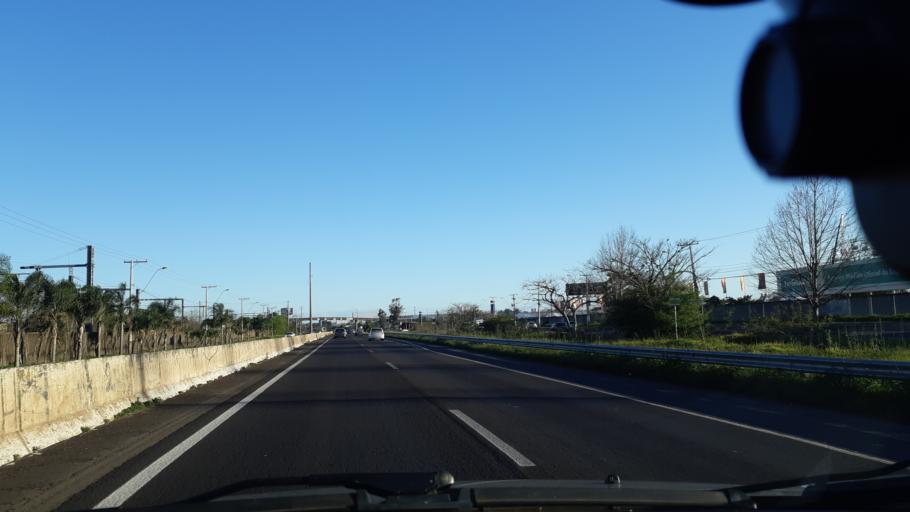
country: BR
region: Rio Grande do Sul
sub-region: Esteio
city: Esteio
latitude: -29.8554
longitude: -51.1803
